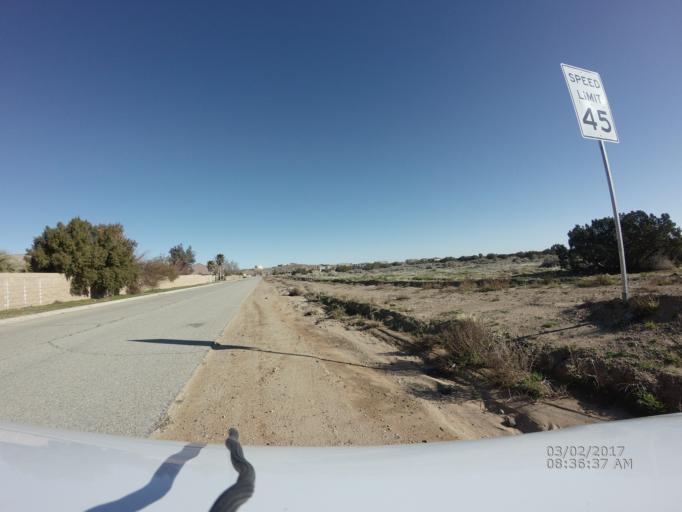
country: US
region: California
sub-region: Los Angeles County
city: Quartz Hill
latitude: 34.6315
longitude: -118.2012
